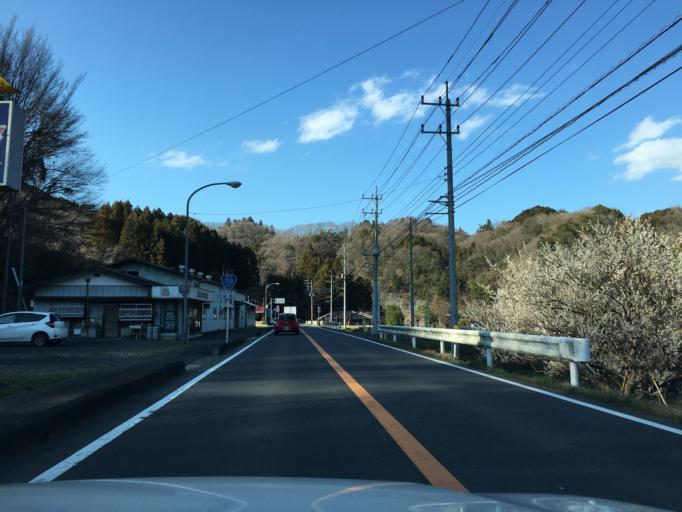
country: JP
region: Ibaraki
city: Daigo
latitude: 36.7334
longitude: 140.3900
